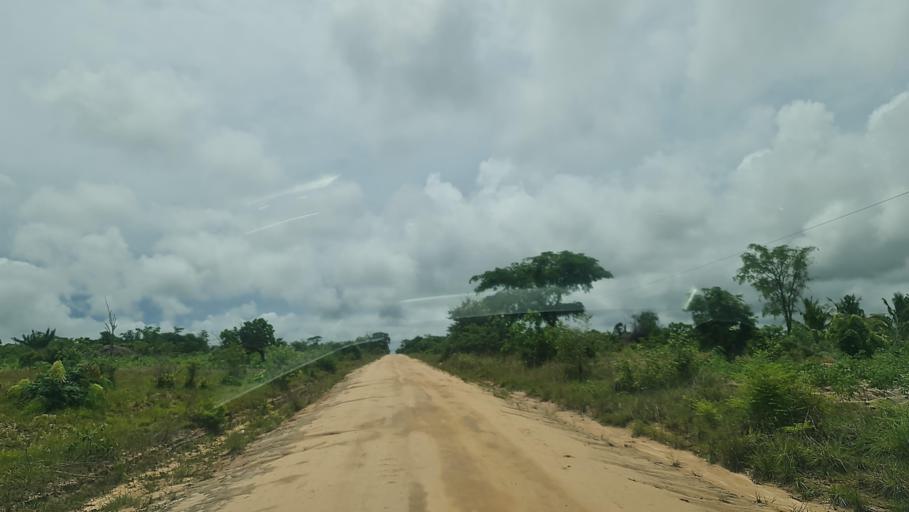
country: MZ
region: Zambezia
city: Quelimane
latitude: -17.2525
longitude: 37.2207
